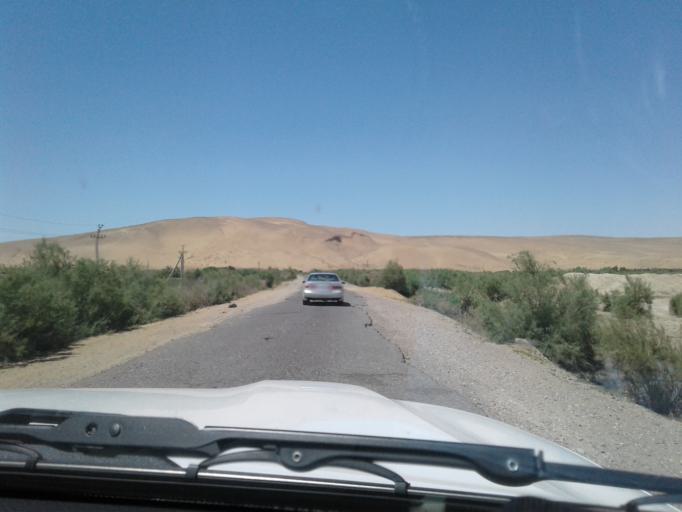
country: AF
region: Badghis
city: Bala Murghab
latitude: 35.9599
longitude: 62.9069
